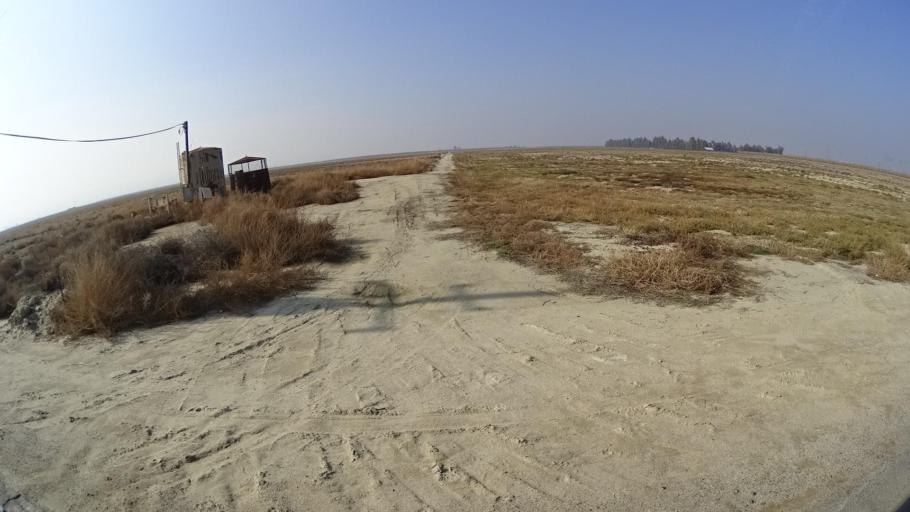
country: US
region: California
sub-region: Kern County
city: Buttonwillow
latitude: 35.3514
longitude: -119.3591
